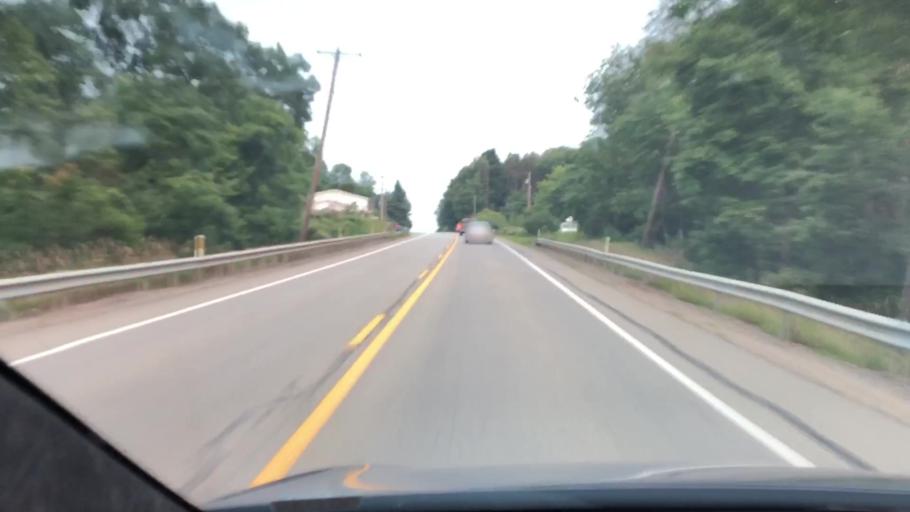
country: US
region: Pennsylvania
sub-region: Butler County
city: Shanor-Northvue
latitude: 40.9139
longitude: -79.9390
